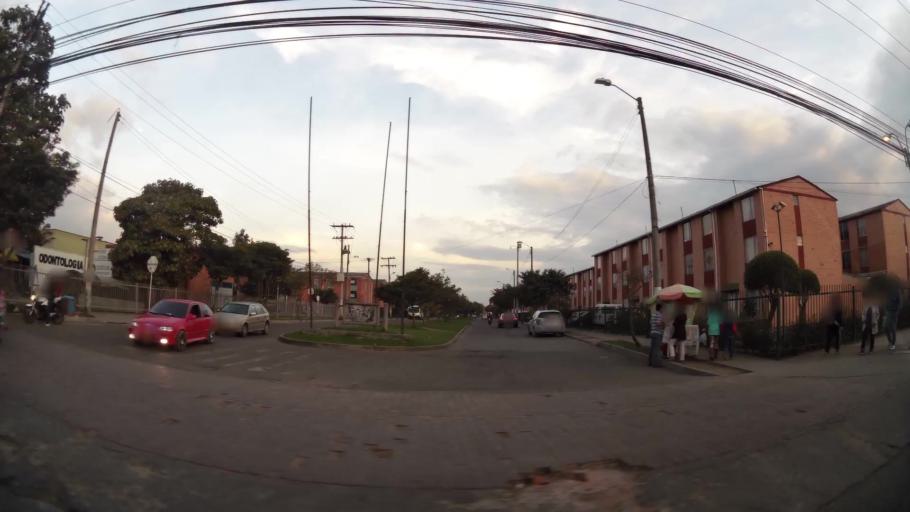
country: CO
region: Cundinamarca
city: Mosquera
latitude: 4.7109
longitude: -74.2237
